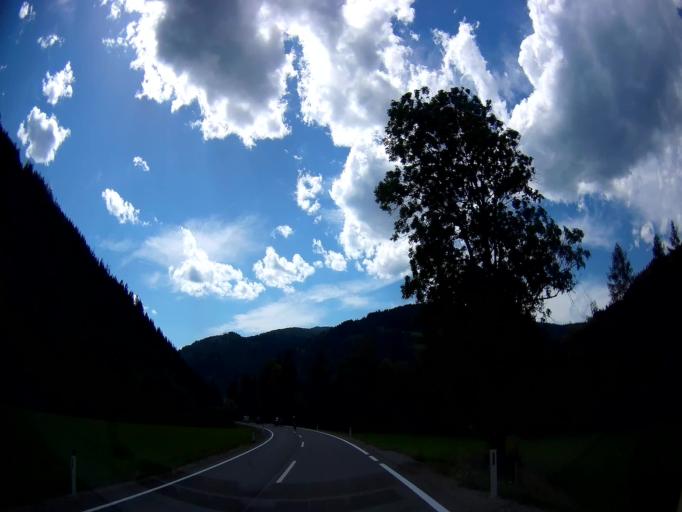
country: AT
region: Styria
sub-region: Politischer Bezirk Murau
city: Stadl an der Mur
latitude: 47.0845
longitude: 13.9497
